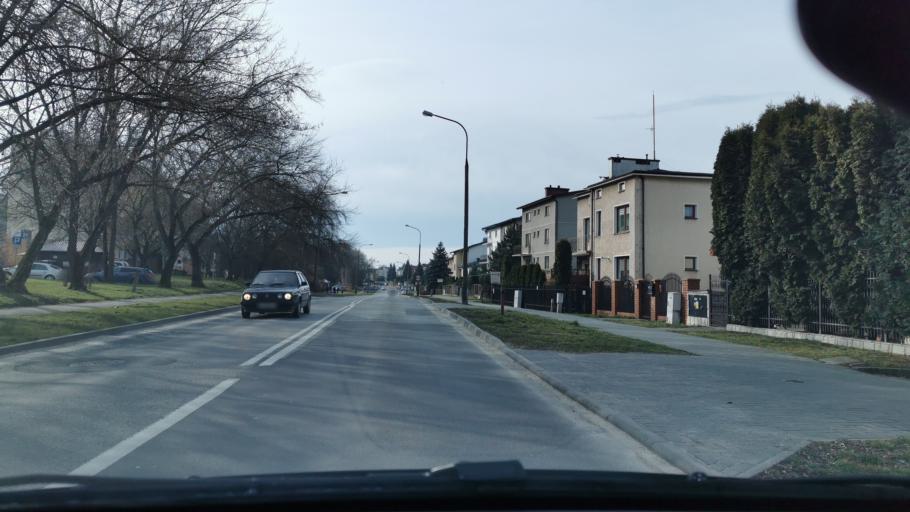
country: PL
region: Lublin Voivodeship
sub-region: Powiat lubelski
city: Lublin
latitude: 51.2122
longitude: 22.5426
